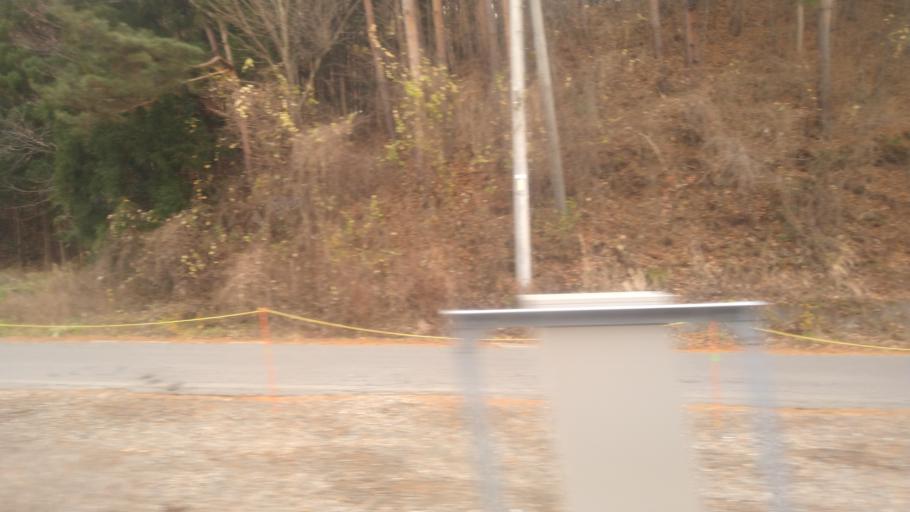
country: JP
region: Nagano
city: Ueda
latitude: 36.4557
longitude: 138.0788
